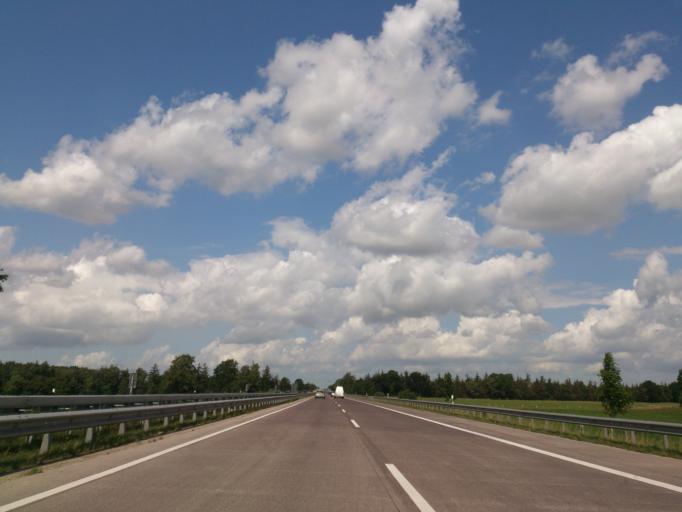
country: DE
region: Schleswig-Holstein
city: Klein Offenseth-Sparrieshoop
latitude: 53.8105
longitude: 9.6692
